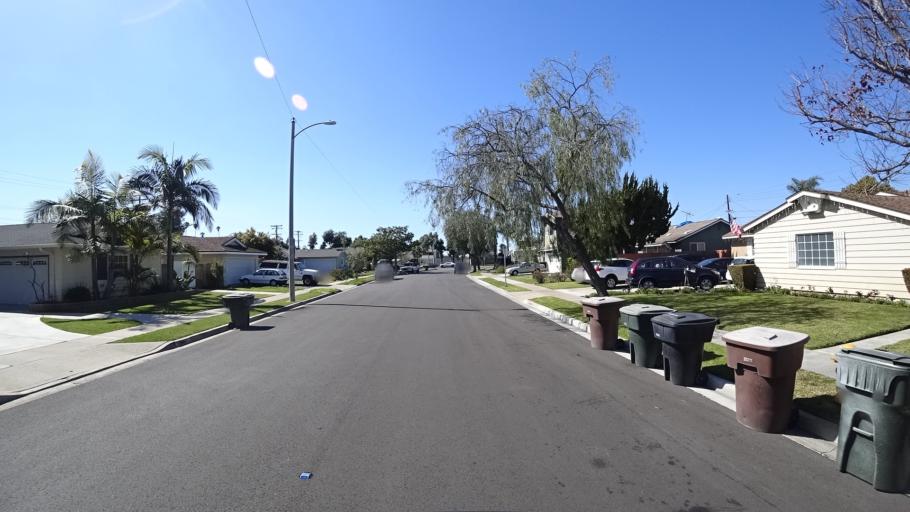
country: US
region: California
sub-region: Orange County
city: Stanton
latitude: 33.8333
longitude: -117.9880
